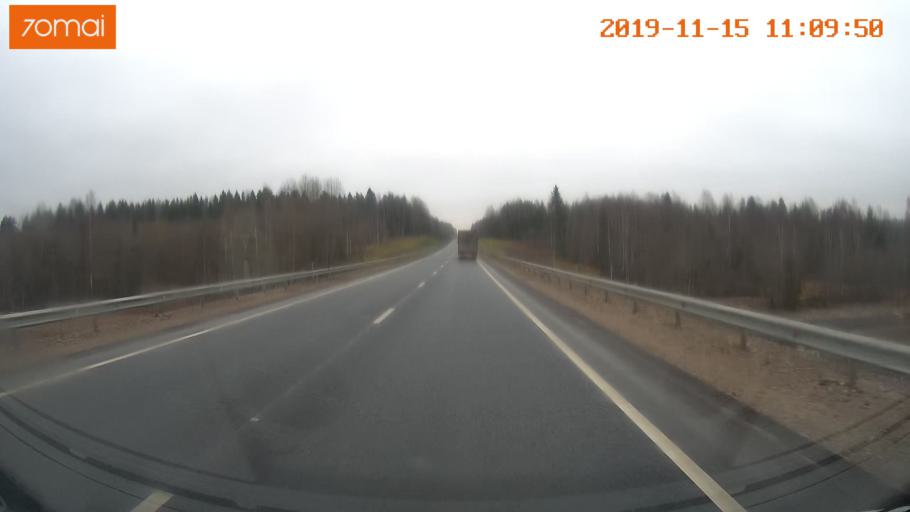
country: RU
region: Vologda
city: Chebsara
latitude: 59.1206
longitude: 39.1073
